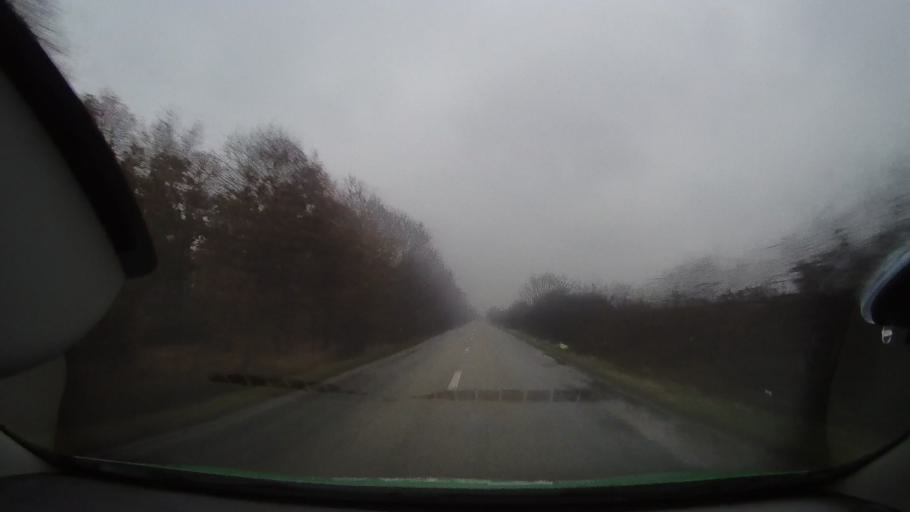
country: RO
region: Bihor
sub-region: Comuna Tinca
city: Gurbediu
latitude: 46.7901
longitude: 21.8308
